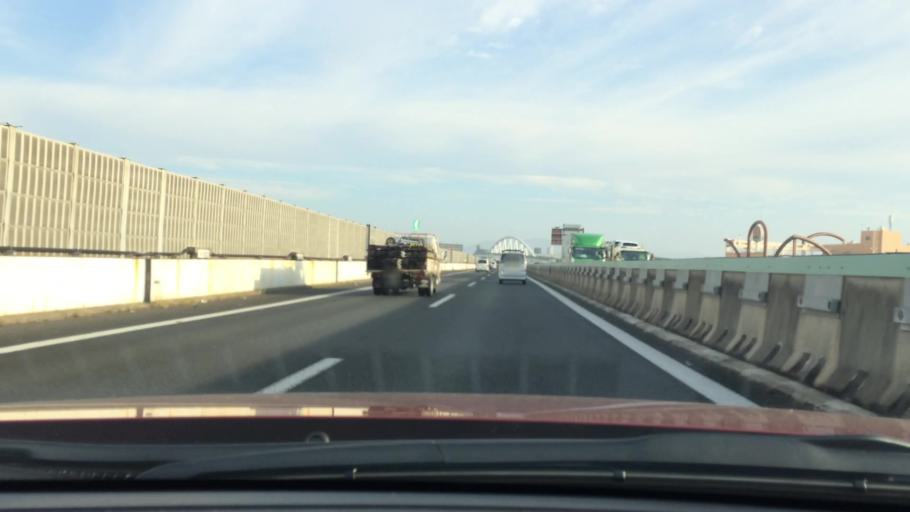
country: JP
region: Osaka
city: Ibaraki
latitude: 34.7902
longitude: 135.5644
